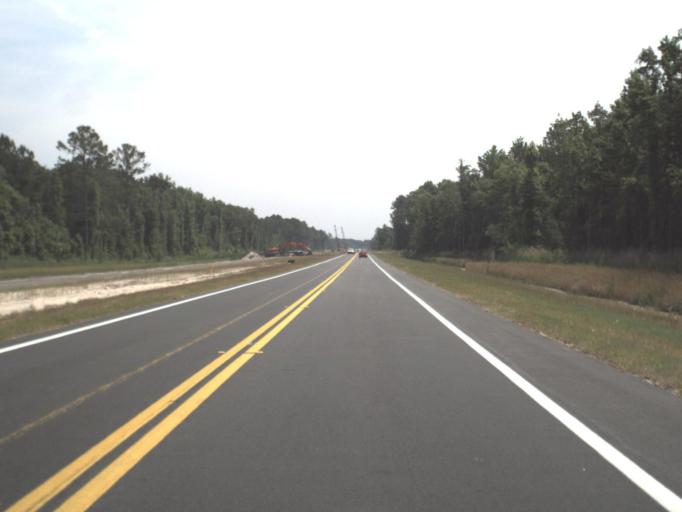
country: US
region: Florida
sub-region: Nassau County
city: Callahan
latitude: 30.5371
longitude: -81.8546
